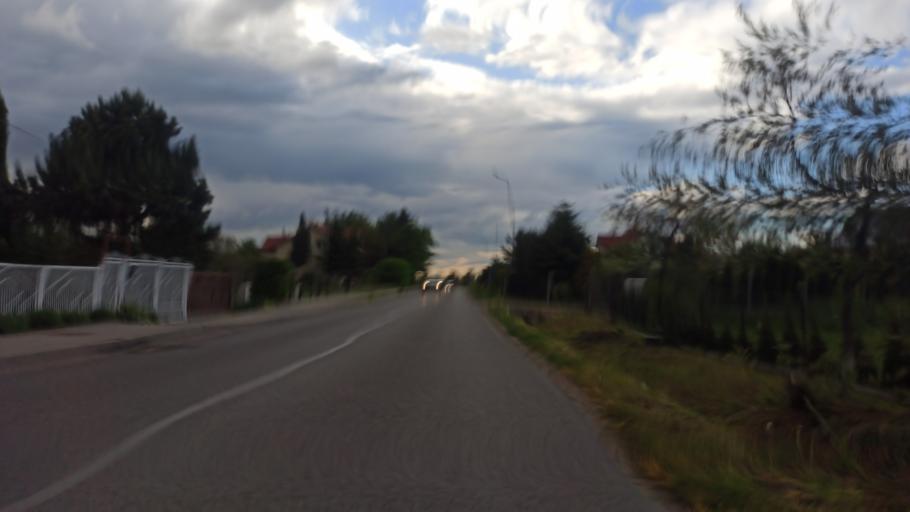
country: PL
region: Subcarpathian Voivodeship
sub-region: Powiat jaroslawski
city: Radymno
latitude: 49.9289
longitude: 22.8443
